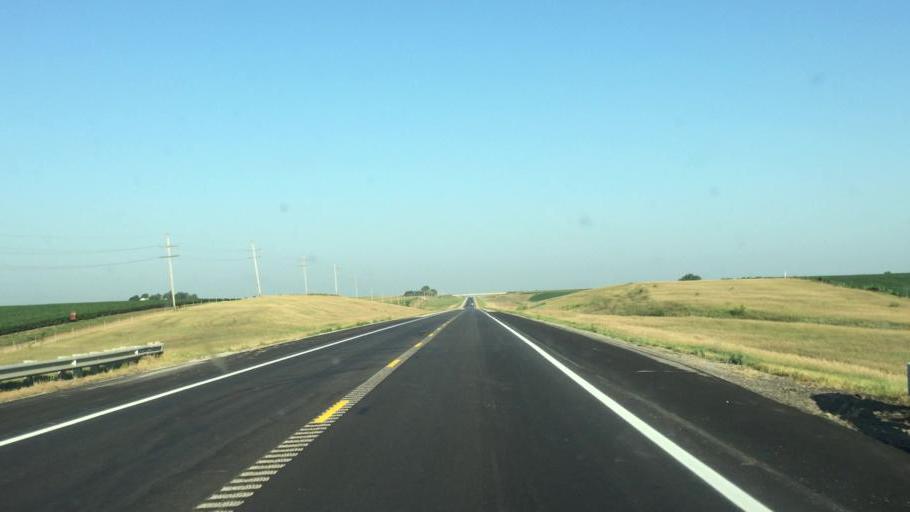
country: US
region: Kansas
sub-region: Brown County
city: Hiawatha
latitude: 39.8421
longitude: -95.4349
